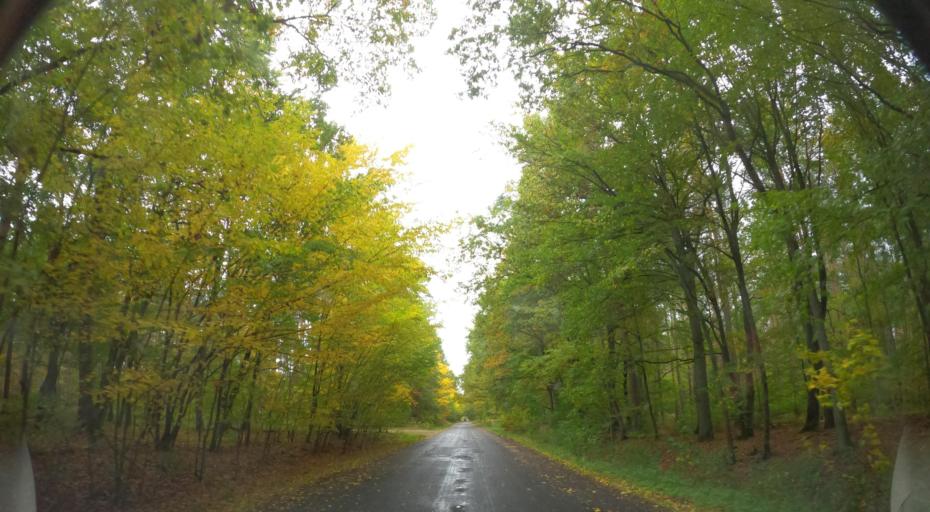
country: PL
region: West Pomeranian Voivodeship
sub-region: Powiat goleniowski
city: Stepnica
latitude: 53.6731
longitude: 14.6692
